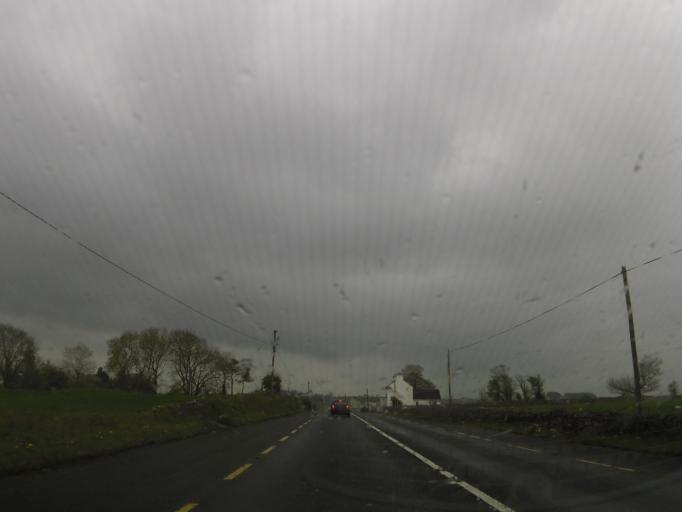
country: IE
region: Connaught
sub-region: County Galway
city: Tuam
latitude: 53.4865
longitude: -8.9089
